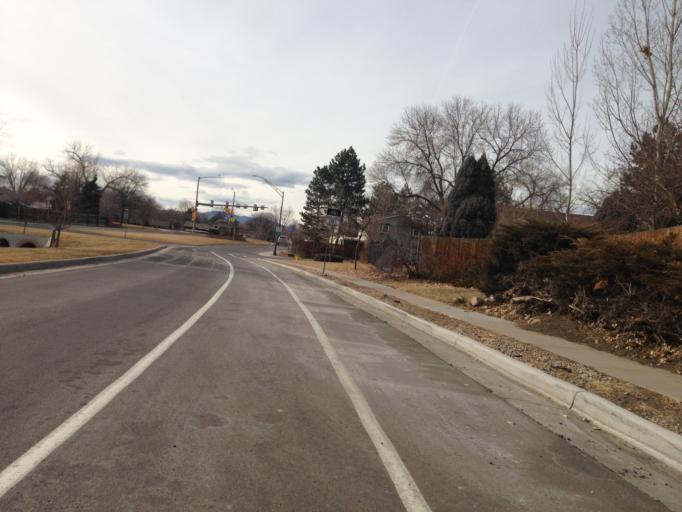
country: US
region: Colorado
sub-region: Adams County
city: Westminster
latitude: 39.8472
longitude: -105.0799
